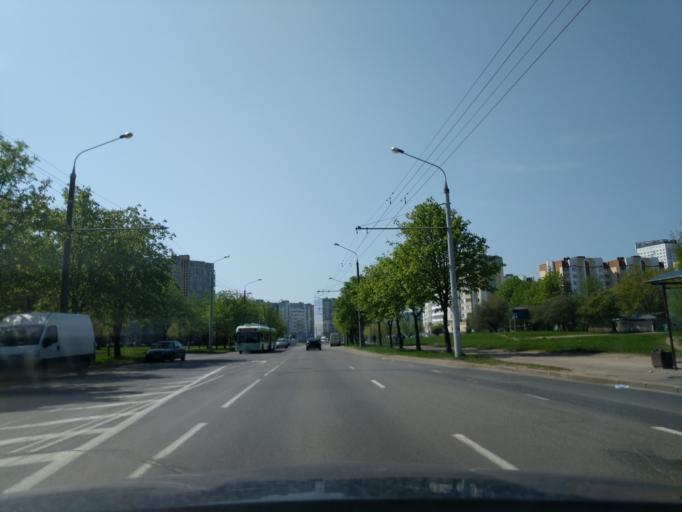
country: BY
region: Minsk
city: Novoye Medvezhino
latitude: 53.8668
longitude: 27.4562
